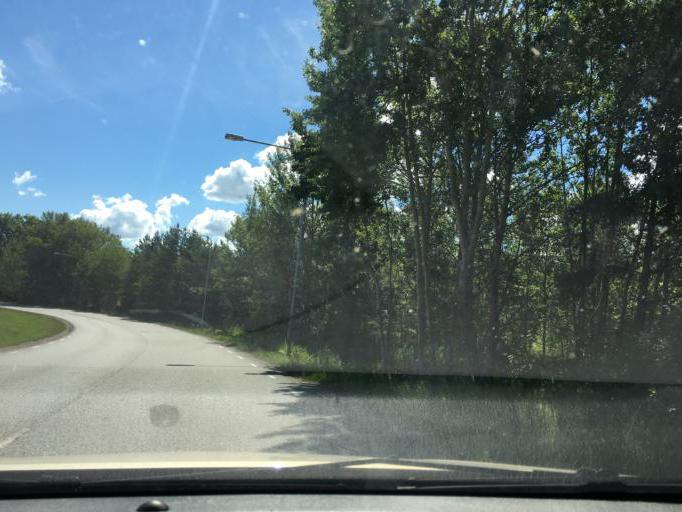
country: SE
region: Stockholm
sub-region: Nacka Kommun
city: Fisksatra
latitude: 59.2916
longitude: 18.2436
